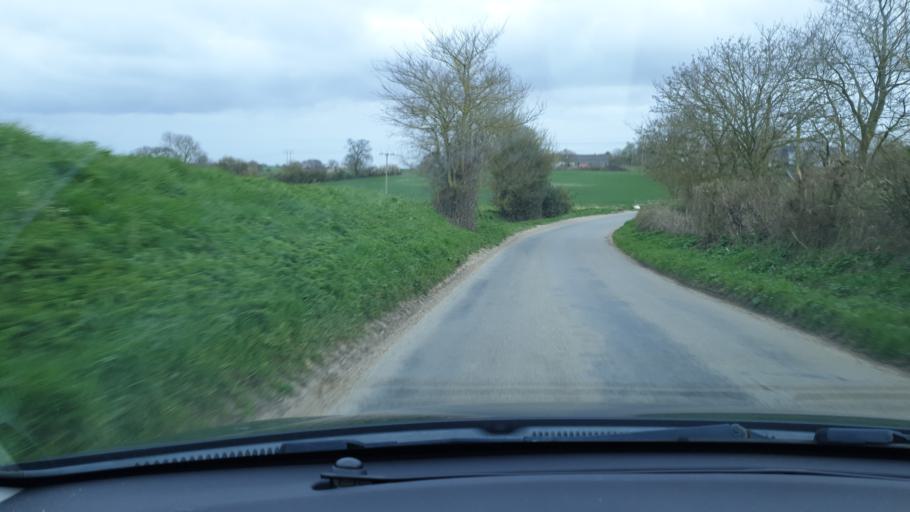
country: GB
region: England
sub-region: Essex
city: Mistley
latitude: 51.9295
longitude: 1.1765
